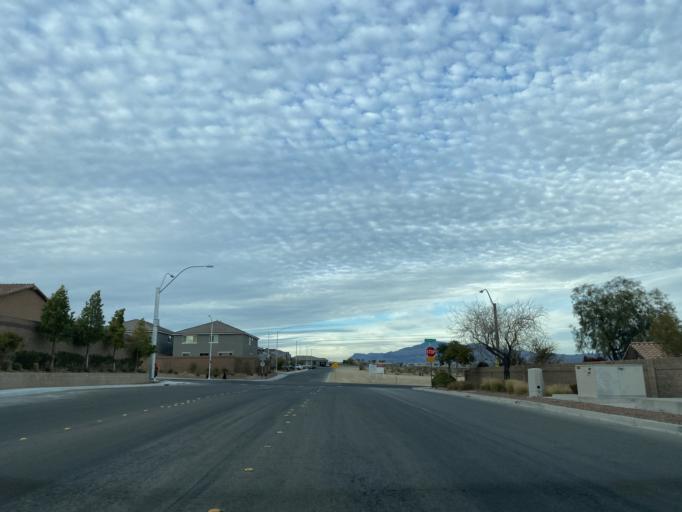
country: US
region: Nevada
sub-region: Clark County
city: Summerlin South
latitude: 36.2766
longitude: -115.3241
